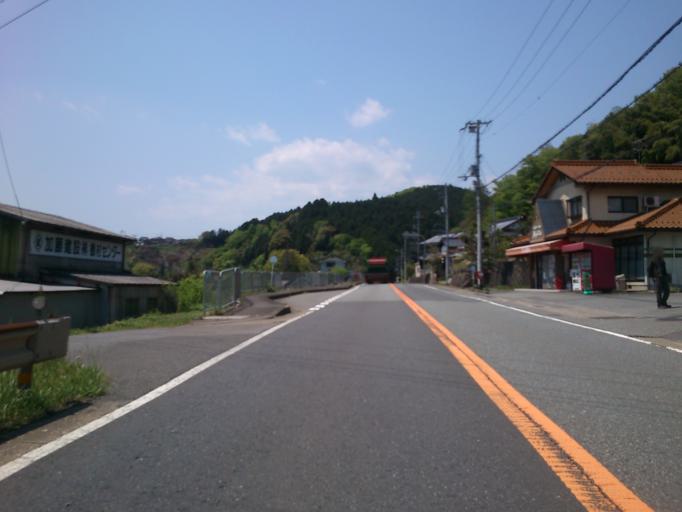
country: JP
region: Kyoto
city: Fukuchiyama
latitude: 35.3258
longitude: 135.0527
